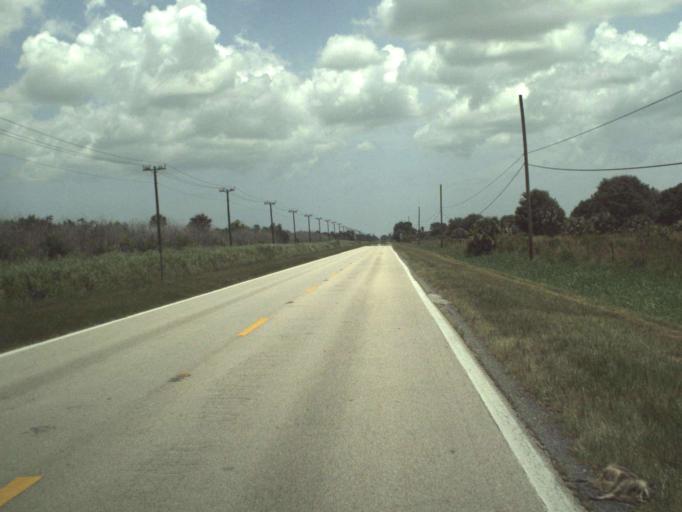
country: US
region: Florida
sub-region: Saint Lucie County
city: Fort Pierce South
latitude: 27.3745
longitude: -80.4627
